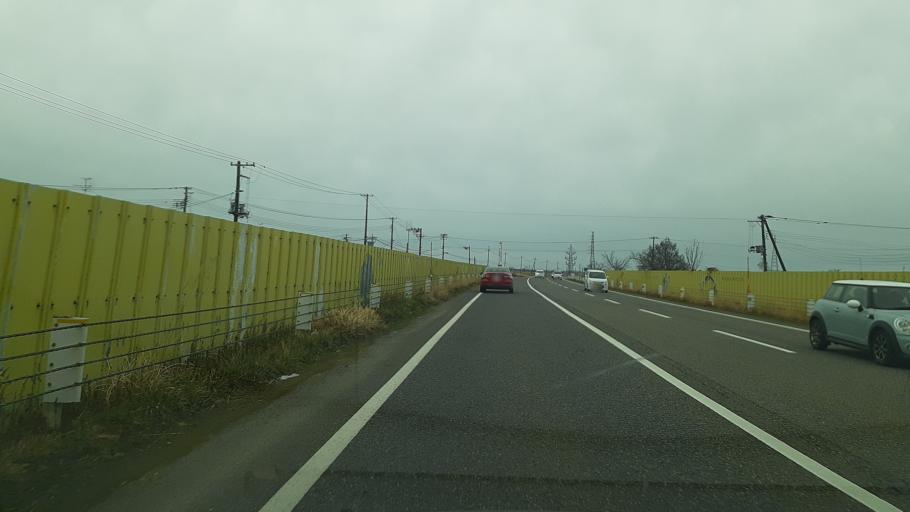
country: JP
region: Niigata
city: Niitsu-honcho
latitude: 37.7981
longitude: 139.1057
